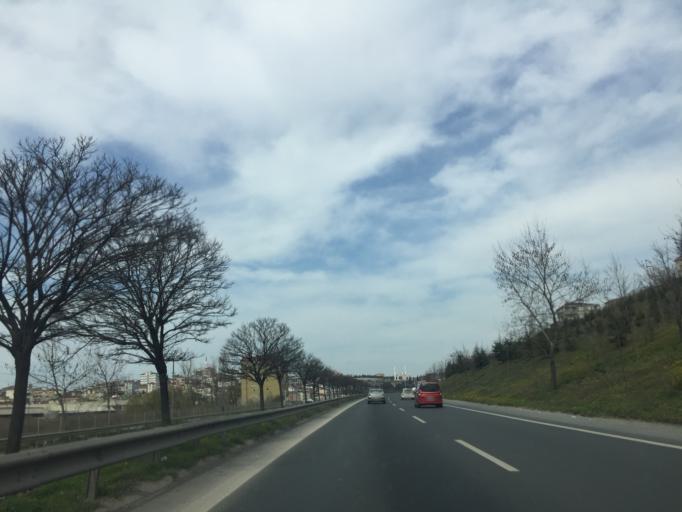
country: TR
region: Kocaeli
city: Darica
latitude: 40.8232
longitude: 29.3649
